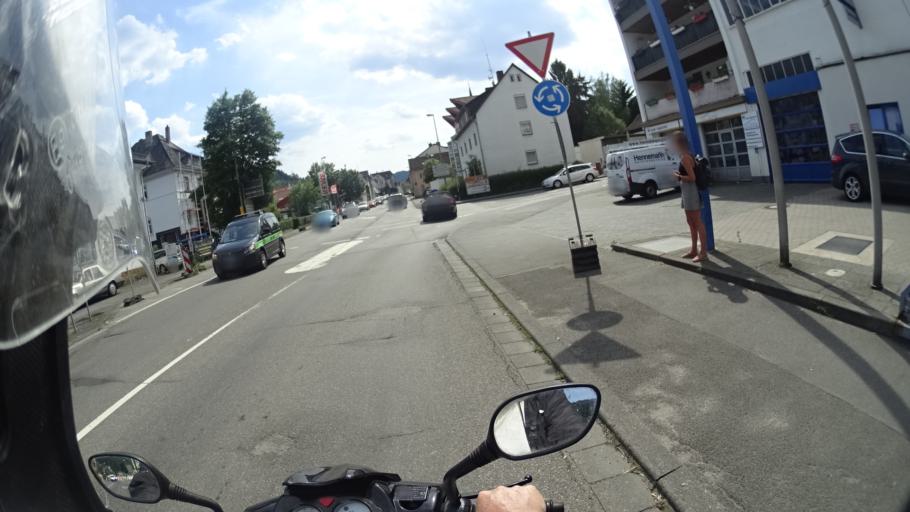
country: DE
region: Hesse
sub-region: Regierungsbezirk Darmstadt
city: Bad Schwalbach
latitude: 50.1469
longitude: 8.0791
